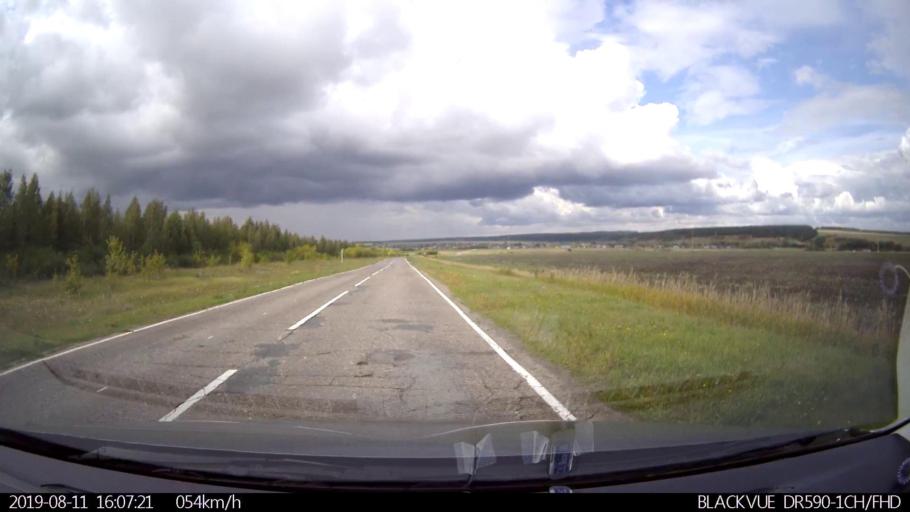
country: RU
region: Ulyanovsk
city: Ignatovka
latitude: 53.9761
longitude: 47.6470
